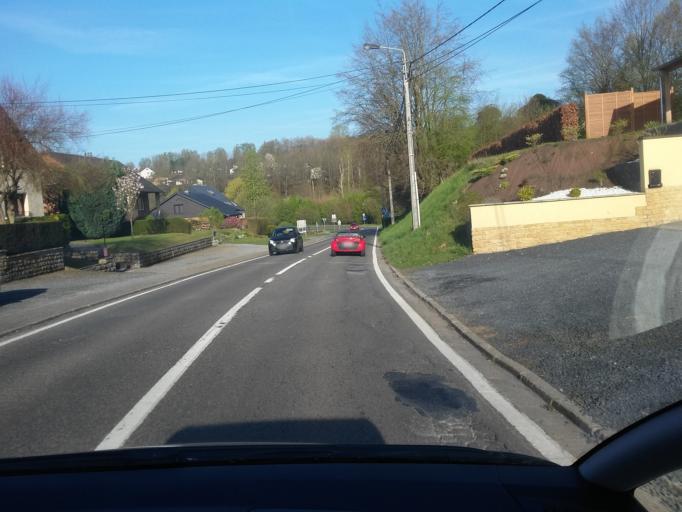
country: BE
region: Wallonia
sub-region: Province du Luxembourg
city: Virton
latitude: 49.5805
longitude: 5.5578
